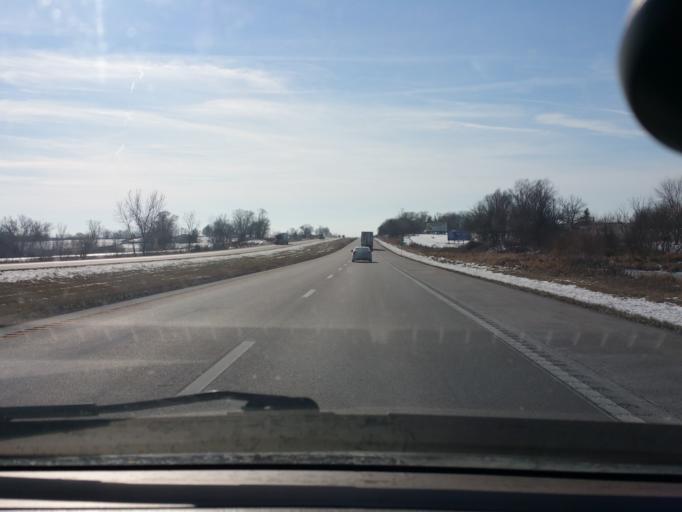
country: US
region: Missouri
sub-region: Clinton County
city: Cameron
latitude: 39.7931
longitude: -94.2038
